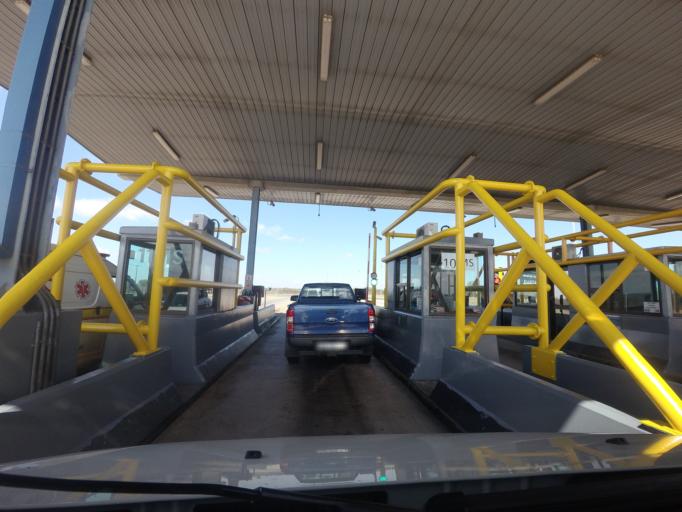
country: ZA
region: Limpopo
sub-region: Vhembe District Municipality
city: Louis Trichardt
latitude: -23.3669
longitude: 29.7751
